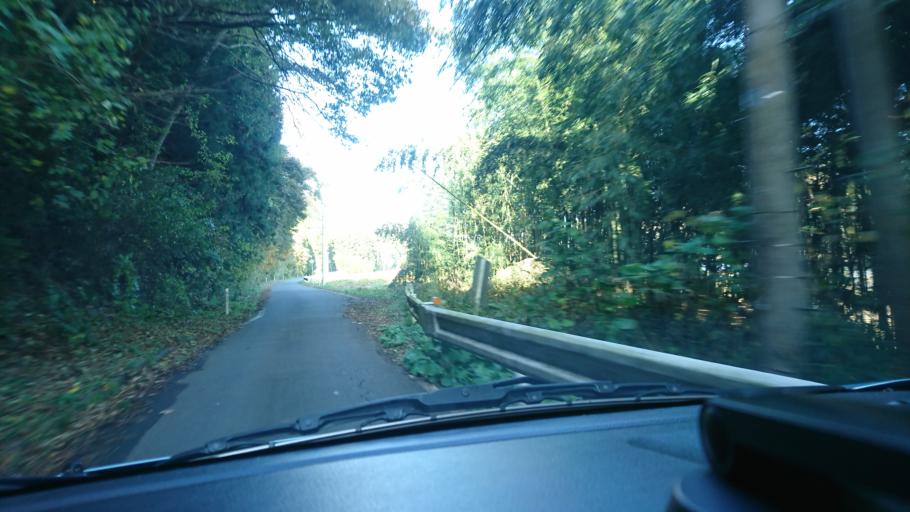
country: JP
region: Iwate
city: Ichinoseki
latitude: 38.8028
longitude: 141.2460
